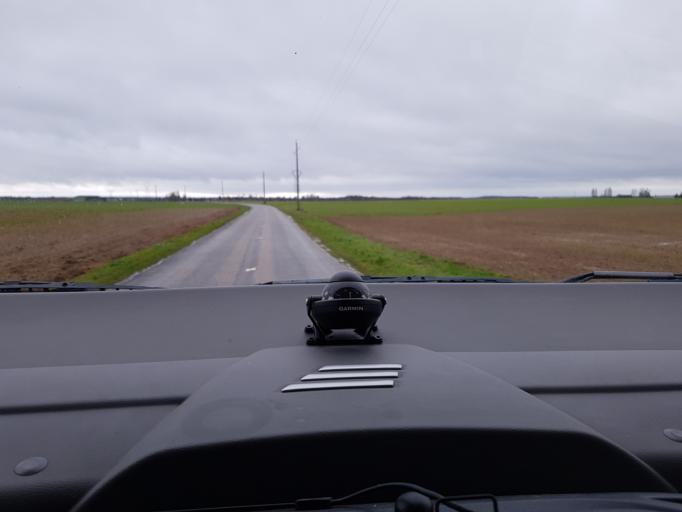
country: FR
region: Haute-Normandie
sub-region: Departement de l'Eure
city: Pont-Saint-Pierre
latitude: 49.2988
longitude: 1.3290
